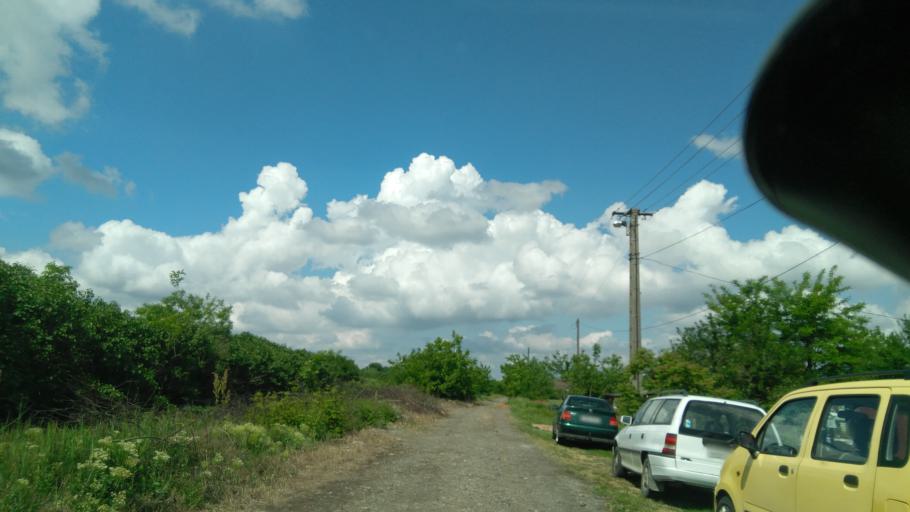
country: HU
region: Bekes
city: Mezobereny
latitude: 46.8335
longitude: 21.0161
